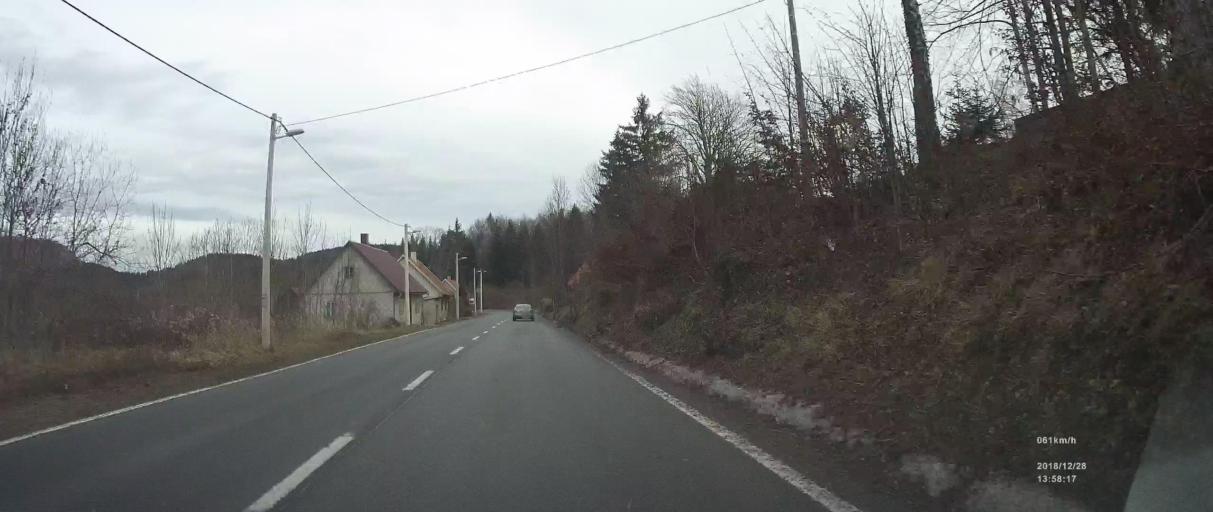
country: HR
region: Primorsko-Goranska
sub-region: Grad Delnice
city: Delnice
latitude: 45.3965
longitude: 14.8972
